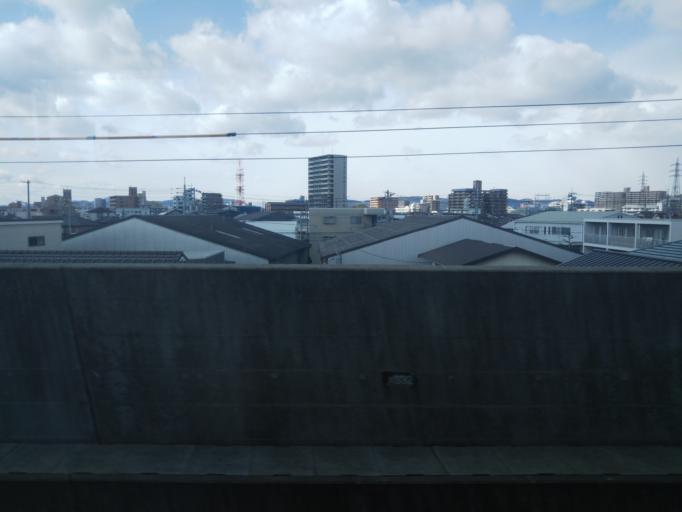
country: JP
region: Okayama
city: Okayama-shi
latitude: 34.6381
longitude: 133.9068
